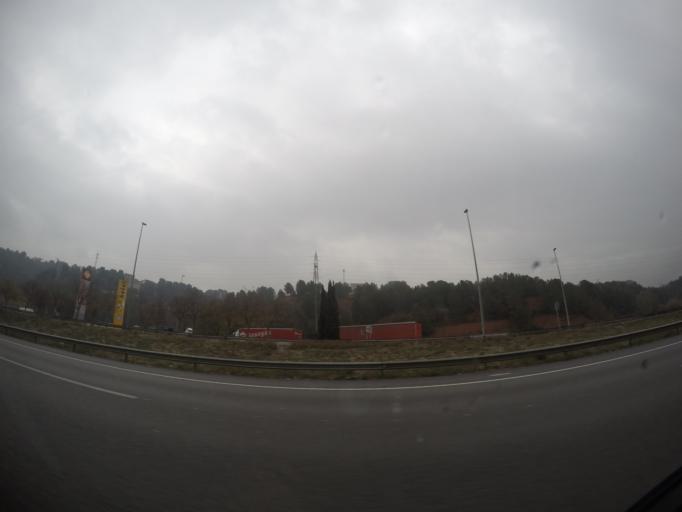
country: ES
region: Catalonia
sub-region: Provincia de Barcelona
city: Castellbisbal
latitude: 41.4639
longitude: 1.9800
